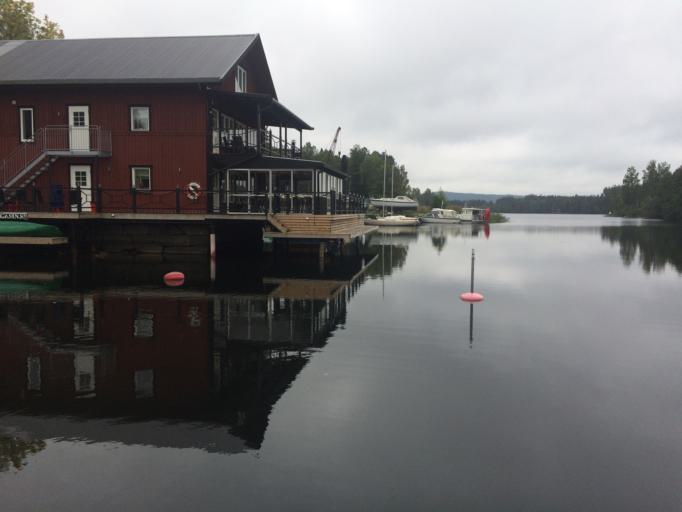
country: SE
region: Vaermland
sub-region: Arjangs Kommun
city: Arjaeng
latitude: 59.1936
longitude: 12.1064
